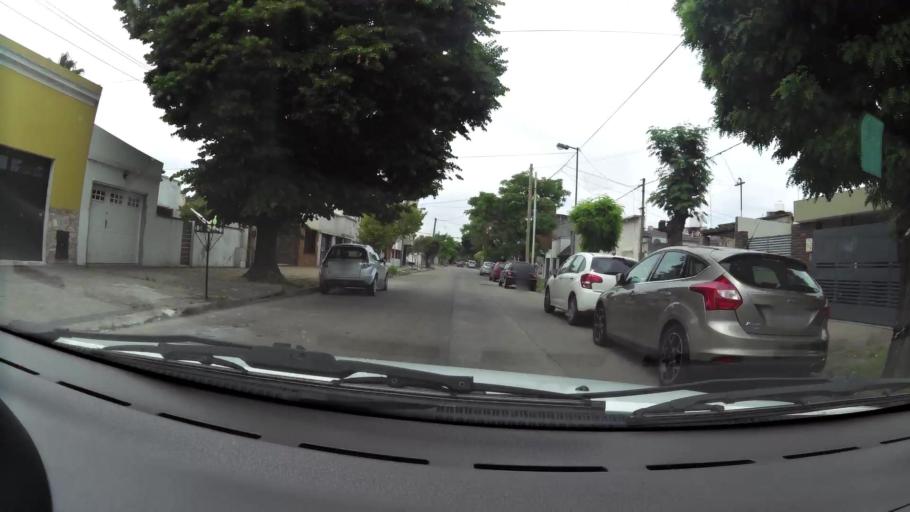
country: AR
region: Buenos Aires
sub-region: Partido de La Plata
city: La Plata
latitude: -34.9368
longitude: -57.9660
